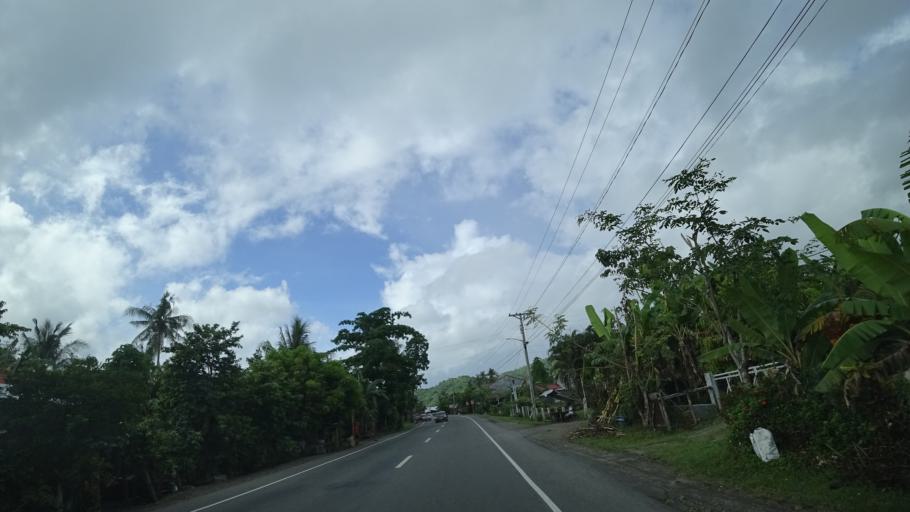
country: PH
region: Eastern Visayas
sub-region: Province of Leyte
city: San Jose
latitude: 11.0143
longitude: 125.0369
